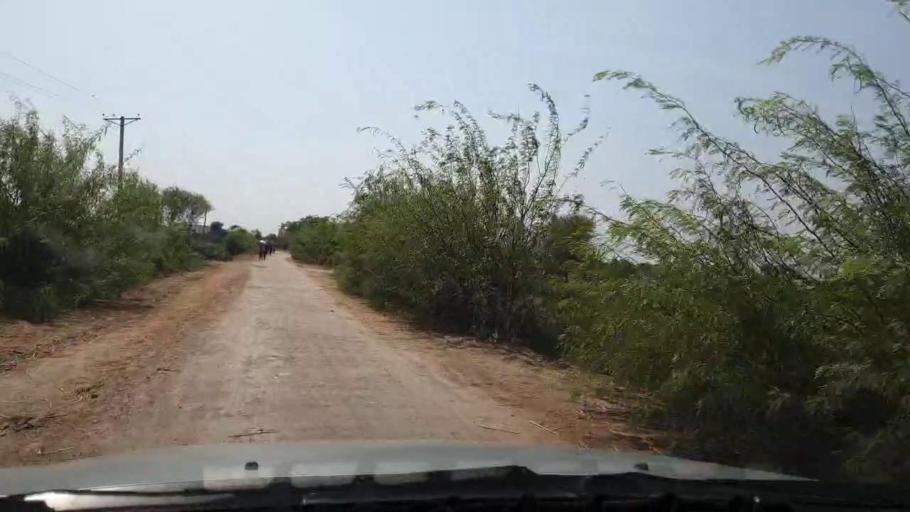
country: PK
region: Sindh
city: Tando Muhammad Khan
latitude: 25.1248
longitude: 68.6202
